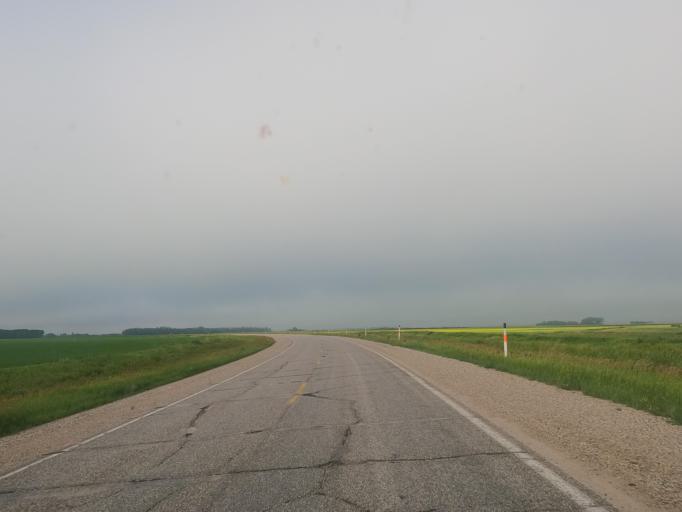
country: CA
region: Manitoba
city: Carman
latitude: 49.6790
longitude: -98.1993
